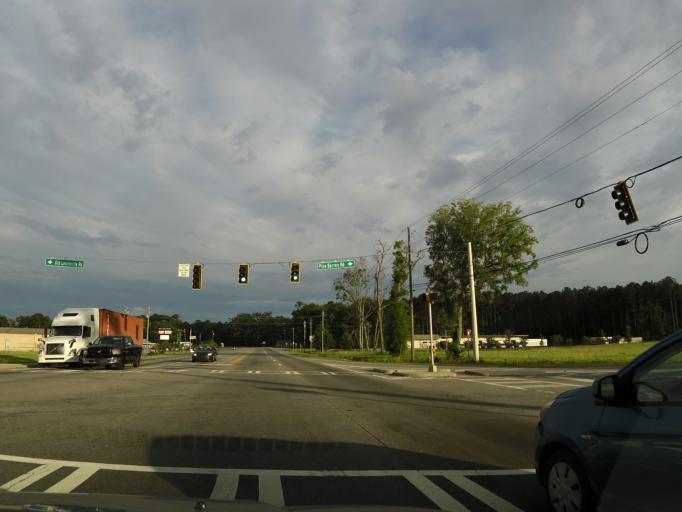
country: US
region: Georgia
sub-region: Chatham County
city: Pooler
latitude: 32.1003
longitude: -81.2221
